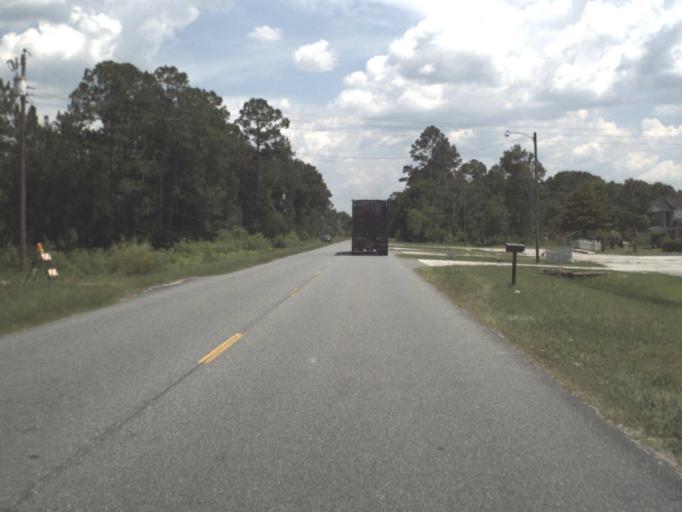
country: US
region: Florida
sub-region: Bradford County
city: Starke
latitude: 30.0389
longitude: -82.0625
